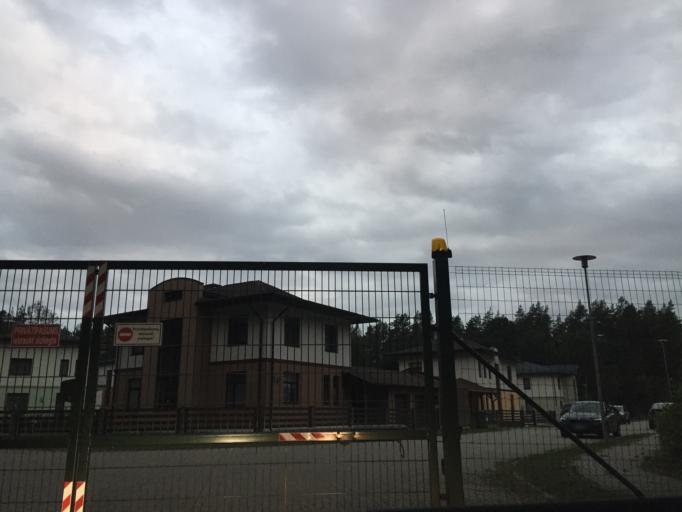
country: LV
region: Stopini
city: Ulbroka
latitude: 56.9568
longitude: 24.2777
